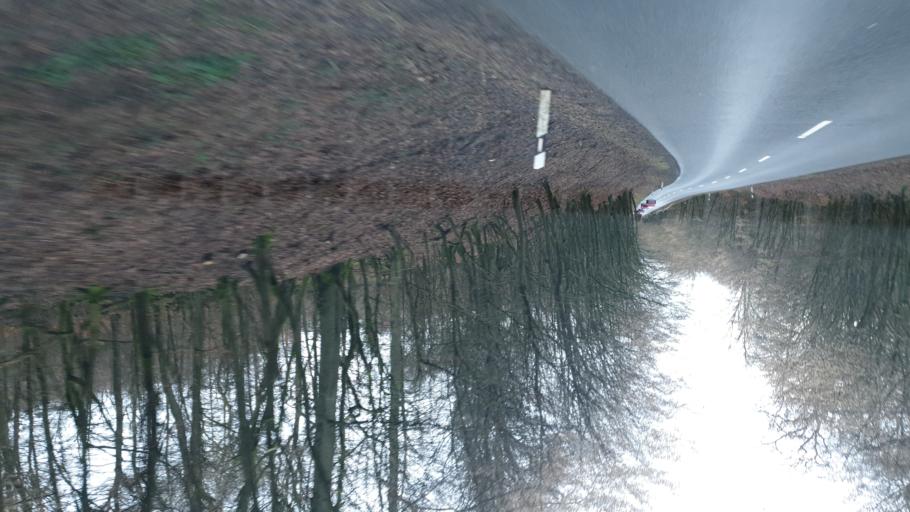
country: DE
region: Hesse
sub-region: Regierungsbezirk Darmstadt
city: Glashutten
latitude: 50.1992
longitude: 8.3521
